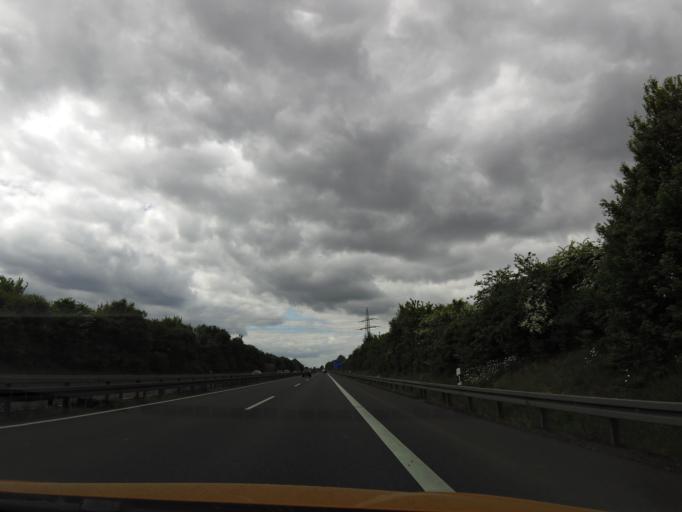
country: DE
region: Lower Saxony
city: Elbe
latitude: 52.1352
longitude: 10.3095
